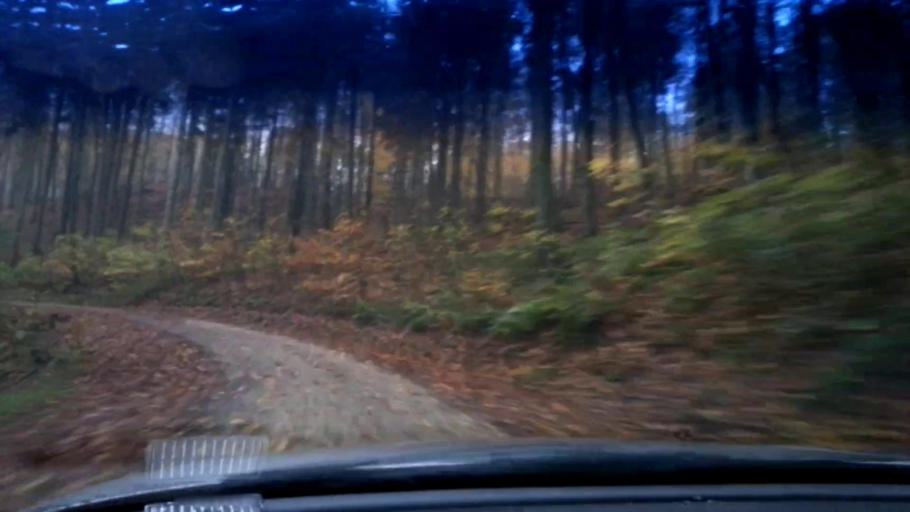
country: DE
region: Bavaria
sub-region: Upper Franconia
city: Litzendorf
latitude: 49.9395
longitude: 11.0296
